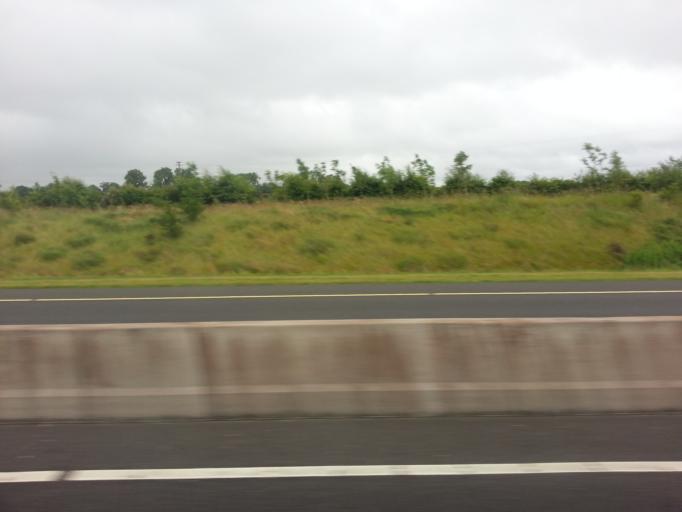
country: IE
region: Leinster
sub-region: Kildare
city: Moone
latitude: 52.9901
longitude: -6.8488
